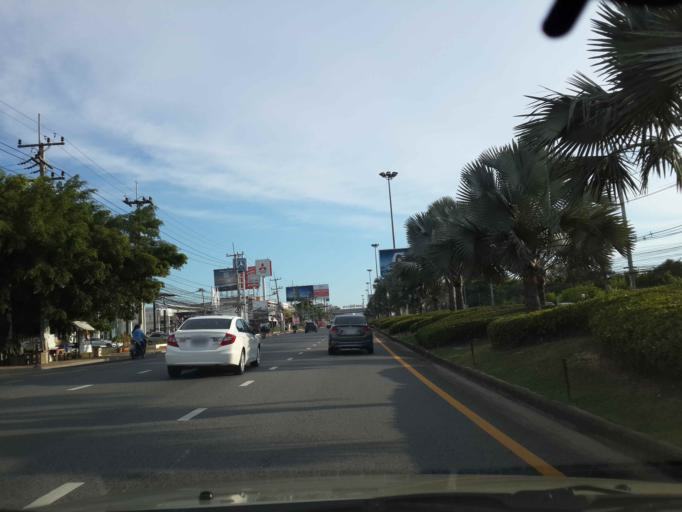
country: TH
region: Chon Buri
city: Bang Lamung
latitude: 12.9877
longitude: 100.9236
